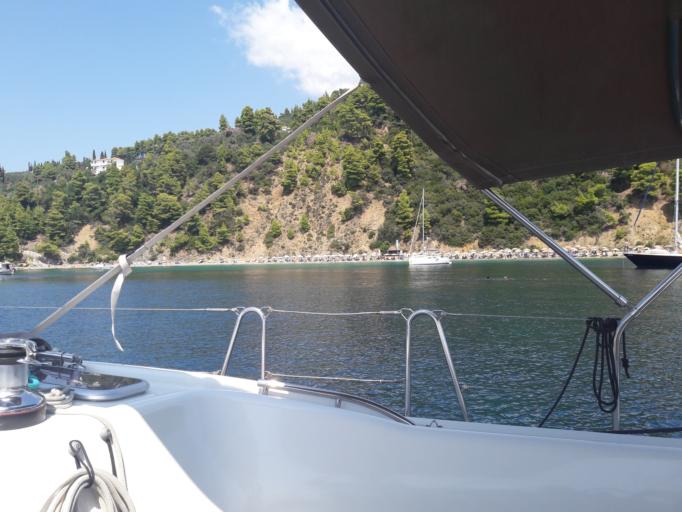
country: GR
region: Thessaly
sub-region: Nomos Magnisias
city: Skopelos
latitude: 39.0841
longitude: 23.7493
